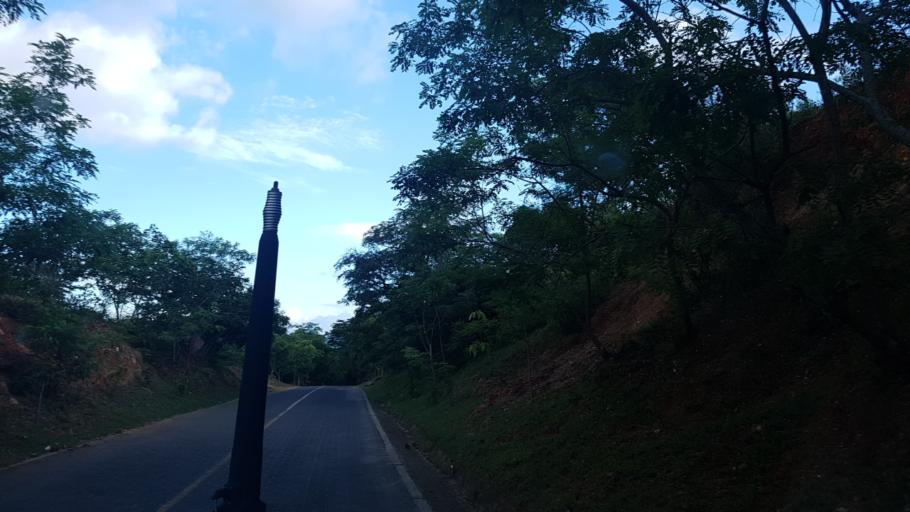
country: NI
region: Nueva Segovia
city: Ocotal
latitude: 13.6474
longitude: -86.6070
